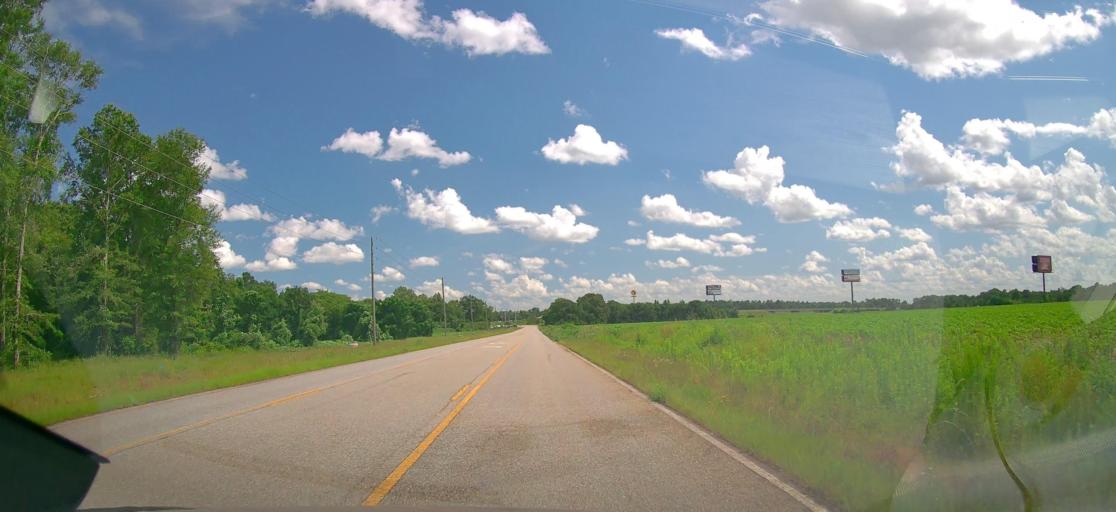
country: US
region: Georgia
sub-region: Houston County
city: Centerville
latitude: 32.5937
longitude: -83.7392
